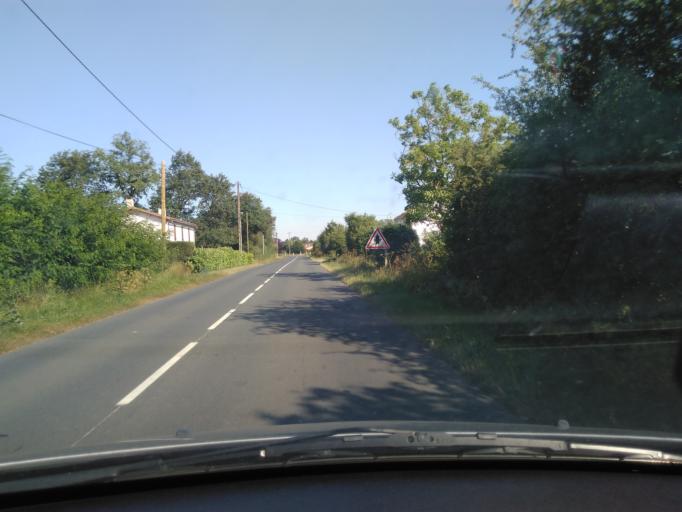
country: FR
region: Pays de la Loire
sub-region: Departement de la Vendee
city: Dompierre-sur-Yon
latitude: 46.7248
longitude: -1.3529
